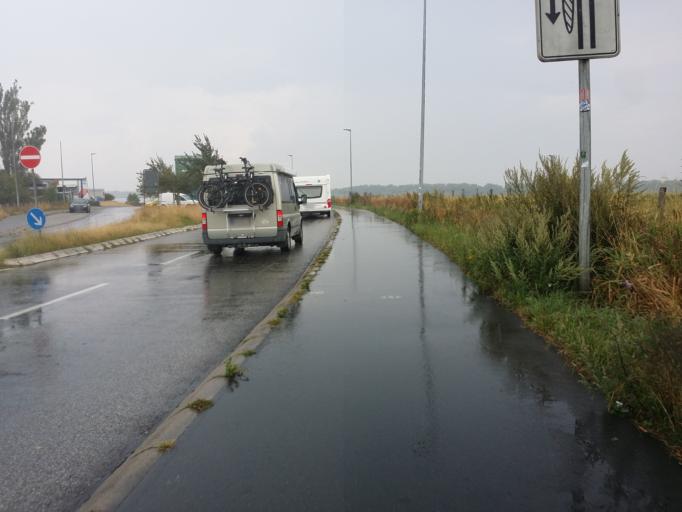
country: DE
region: Schleswig-Holstein
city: Blomesche Wildnis
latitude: 53.7963
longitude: 9.4033
